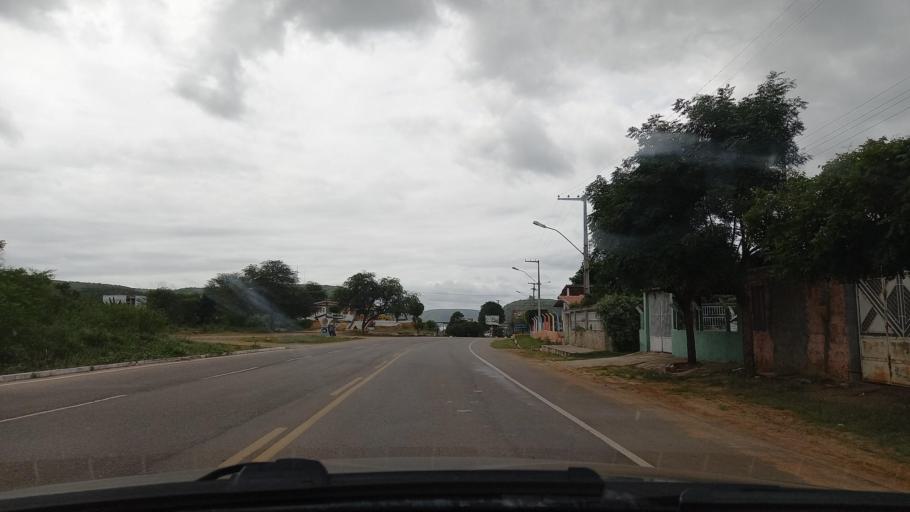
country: BR
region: Sergipe
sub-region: Caninde De Sao Francisco
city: Caninde de Sao Francisco
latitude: -9.6417
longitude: -37.7895
